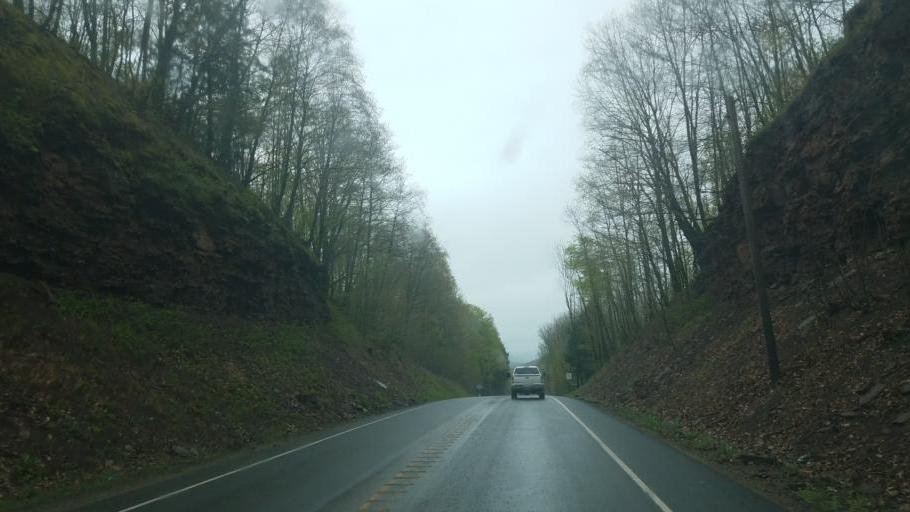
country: US
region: Pennsylvania
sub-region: McKean County
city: Smethport
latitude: 41.8237
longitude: -78.3861
